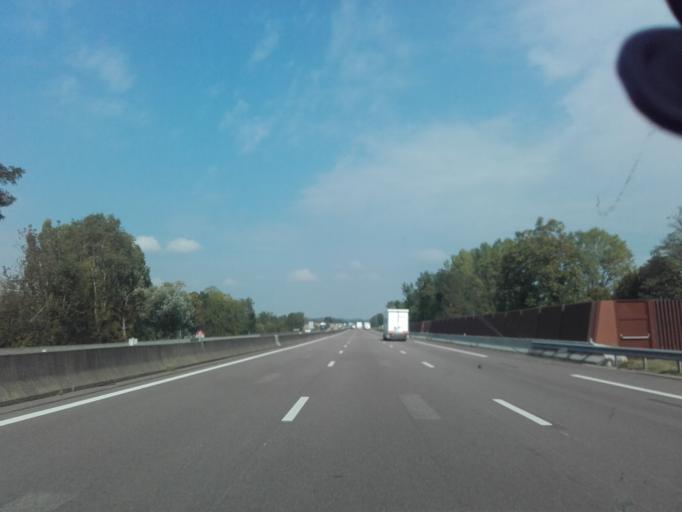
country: FR
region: Rhone-Alpes
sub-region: Departement de l'Ain
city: Pont-de-Vaux
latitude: 46.4720
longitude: 4.8839
